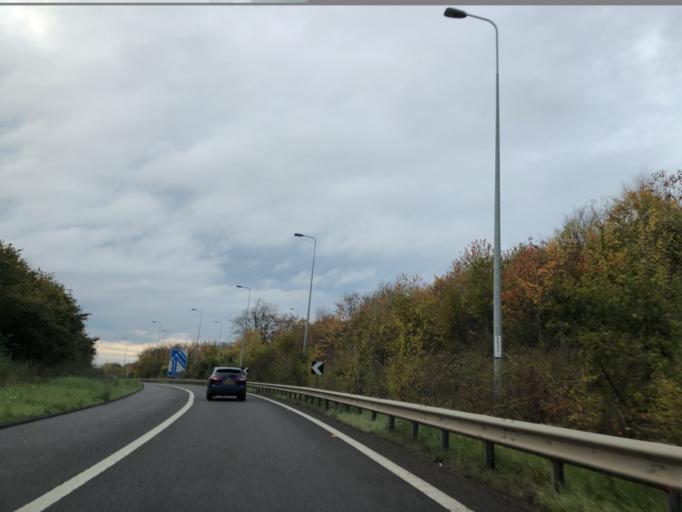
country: GB
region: England
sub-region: Buckinghamshire
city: High Wycombe
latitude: 51.6113
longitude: -0.7692
